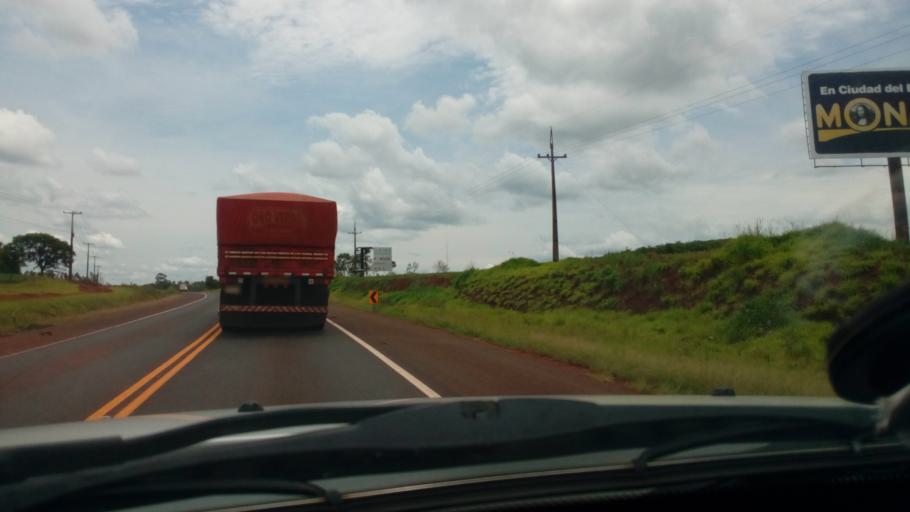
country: PY
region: Alto Parana
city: Colonia Yguazu
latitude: -25.6038
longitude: -54.9353
